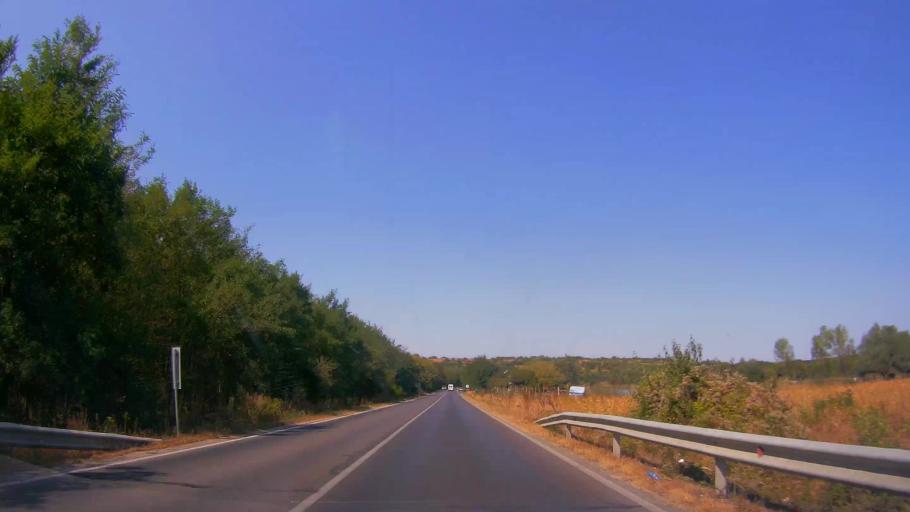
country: BG
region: Razgrad
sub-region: Obshtina Tsar Kaloyan
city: Tsar Kaloyan
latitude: 43.6161
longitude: 26.2144
